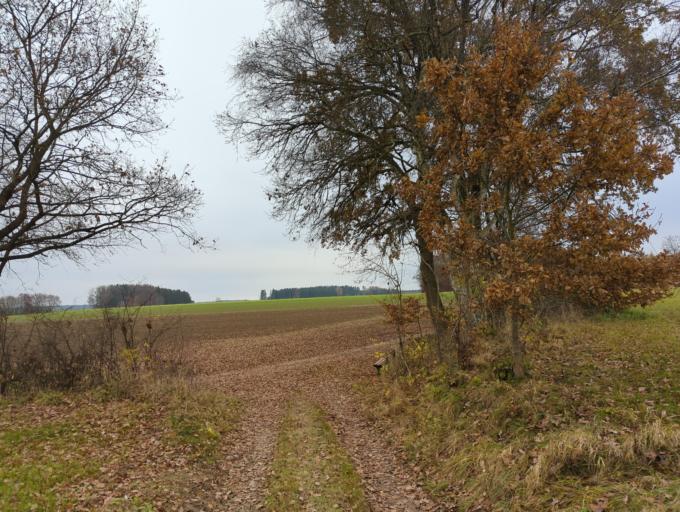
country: DE
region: Bavaria
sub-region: Swabia
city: Rettenbach
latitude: 48.4353
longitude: 10.3213
